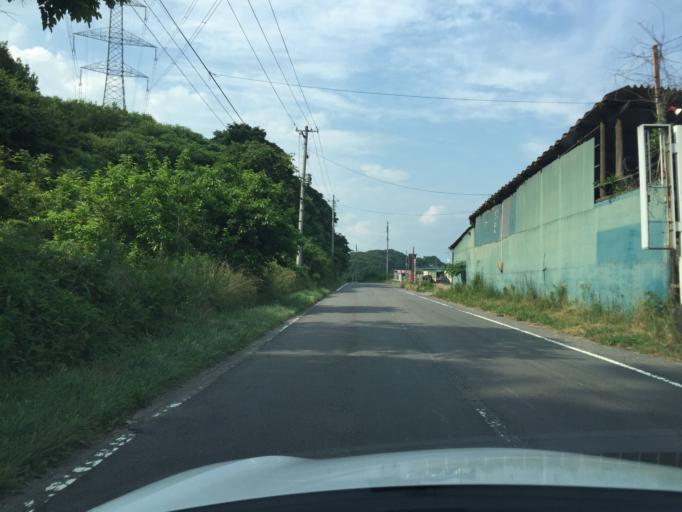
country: JP
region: Fukushima
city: Miharu
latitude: 37.4077
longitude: 140.4503
